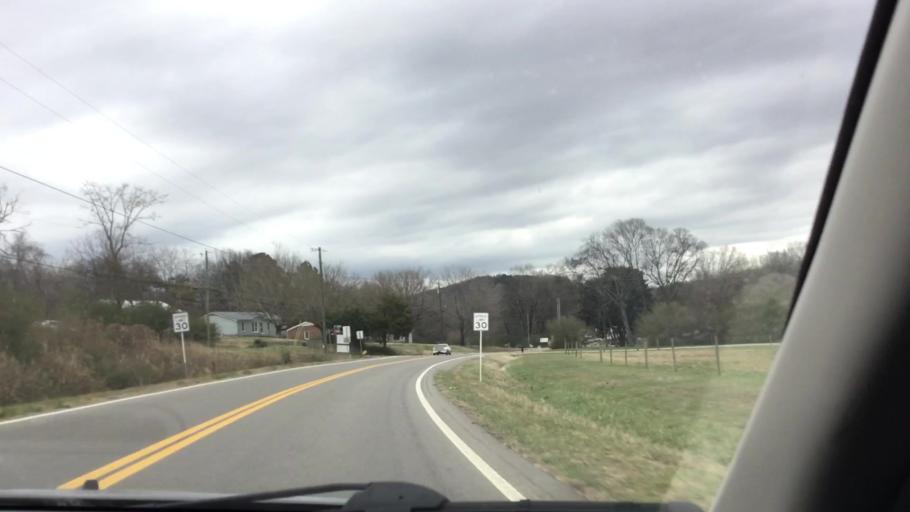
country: US
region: Tennessee
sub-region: Maury County
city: Mount Pleasant
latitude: 35.5950
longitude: -87.2993
